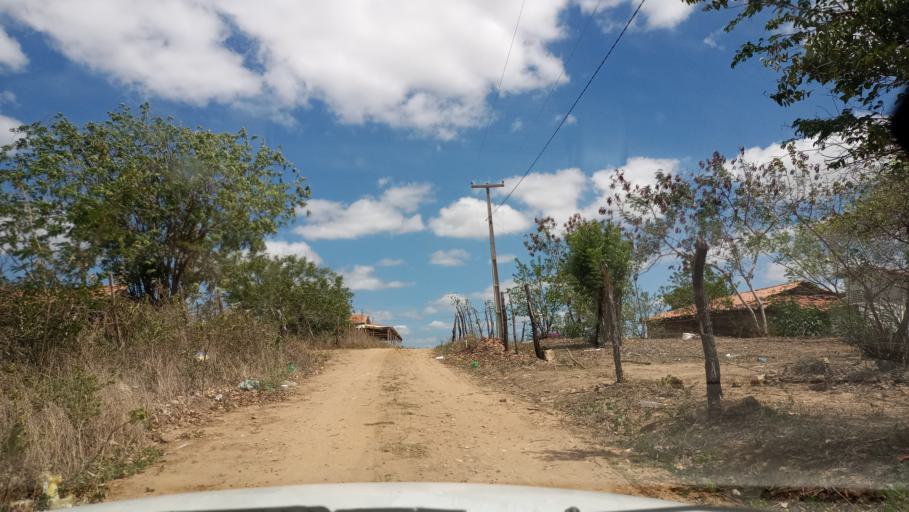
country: BR
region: Rio Grande do Norte
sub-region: Sao Paulo Do Potengi
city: Sao Paulo do Potengi
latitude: -5.7466
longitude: -35.9094
